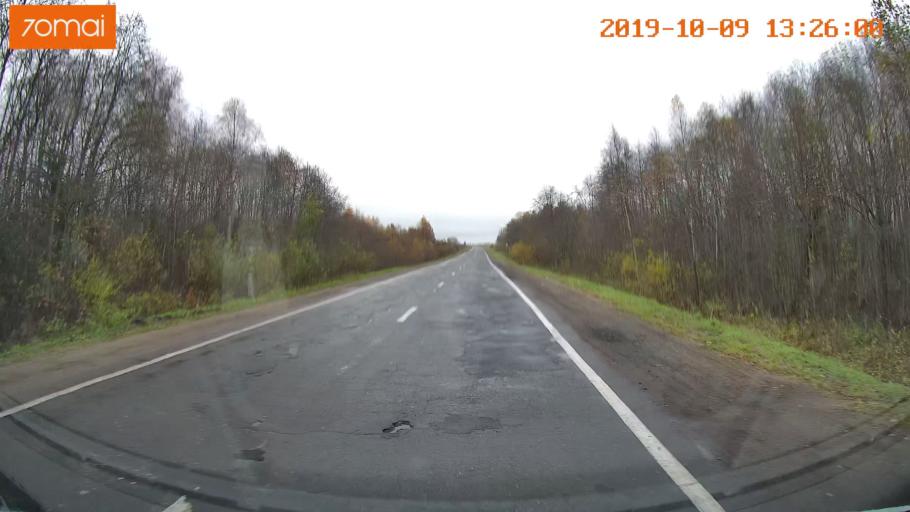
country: RU
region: Jaroslavl
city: Lyubim
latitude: 58.3240
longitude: 40.9191
